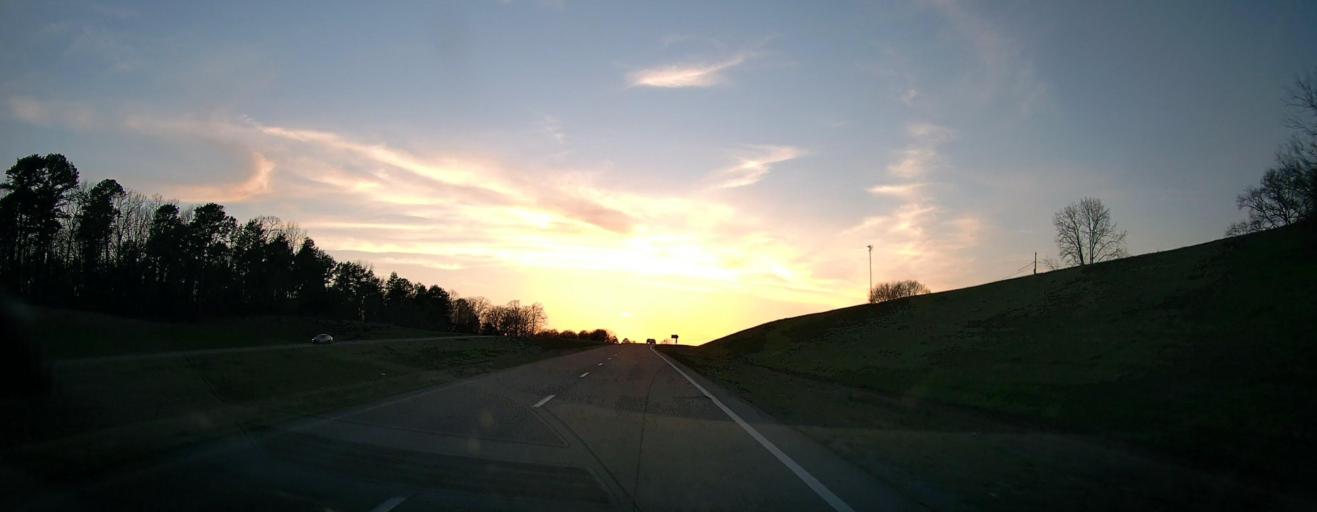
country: US
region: Mississippi
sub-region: Tippah County
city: Ripley
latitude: 34.9463
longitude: -88.7960
